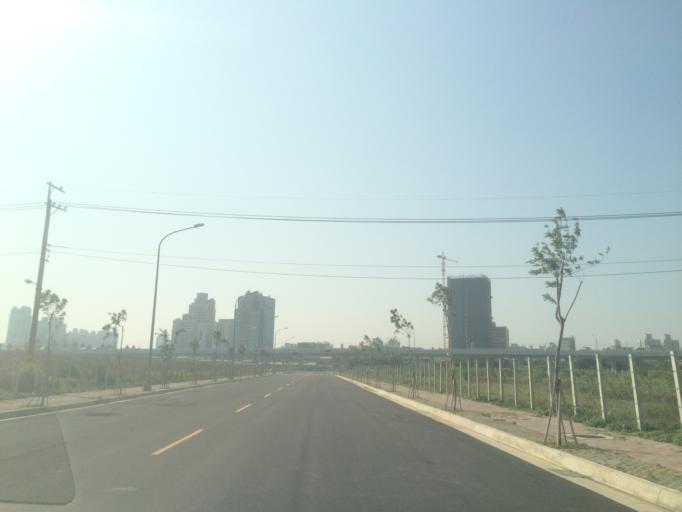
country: TW
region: Taiwan
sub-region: Taichung City
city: Taichung
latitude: 24.1760
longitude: 120.7054
